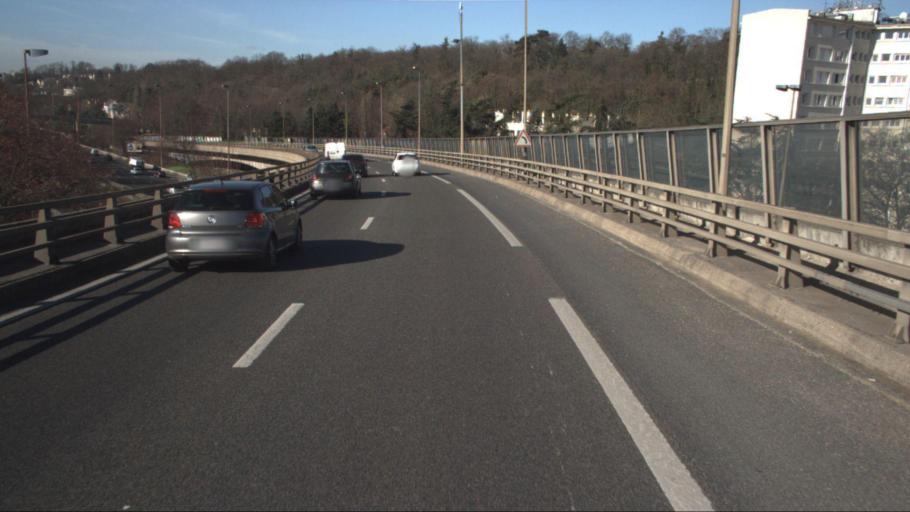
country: FR
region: Ile-de-France
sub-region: Departement du Val-de-Marne
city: Maisons-Alfort
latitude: 48.8166
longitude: 2.4467
